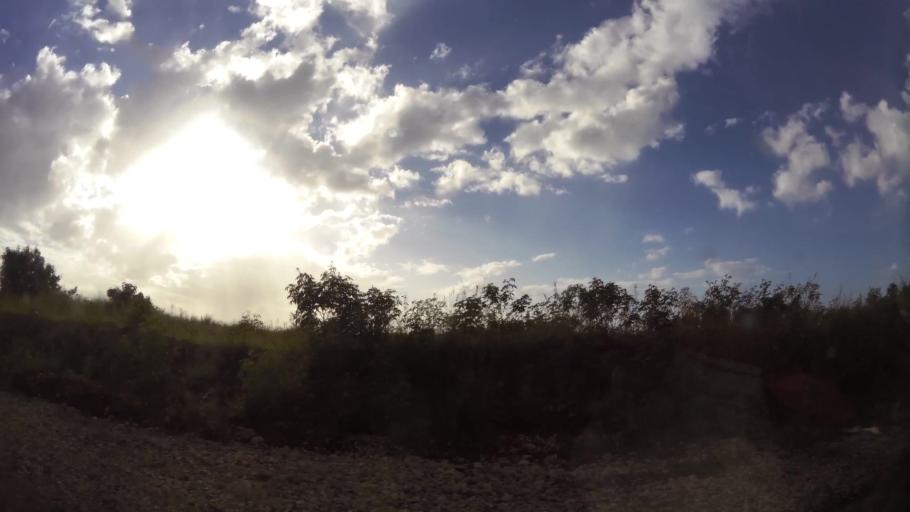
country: DM
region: Saint Paul
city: Mahaut
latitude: 15.3438
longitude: -61.3927
